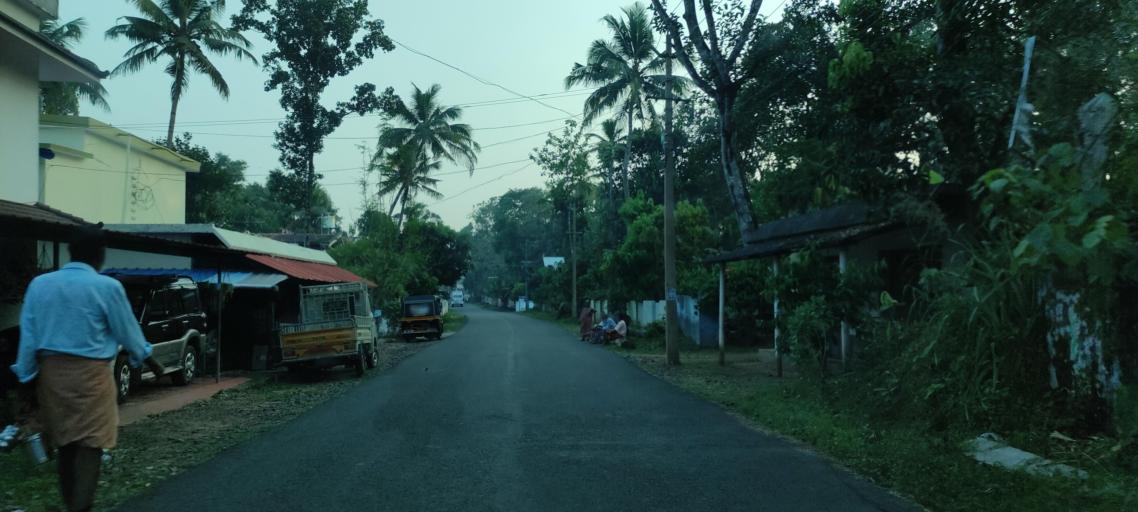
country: IN
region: Kerala
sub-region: Alappuzha
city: Kattanam
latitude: 9.1494
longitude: 76.5754
